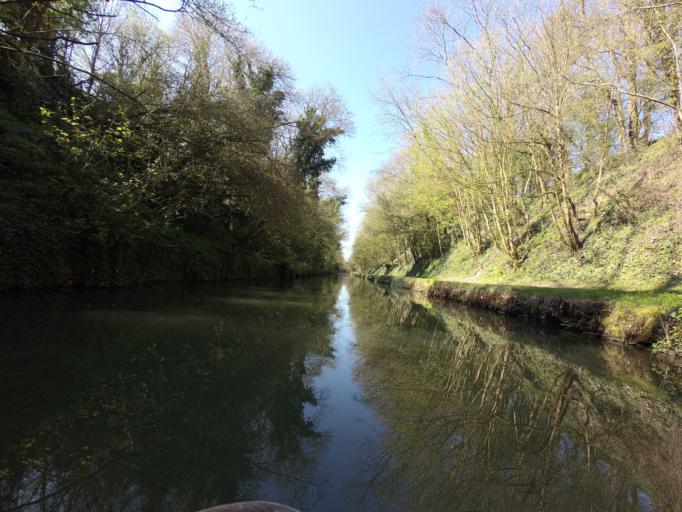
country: GB
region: England
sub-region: Hertfordshire
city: Tring
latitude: 51.8050
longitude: -0.6373
